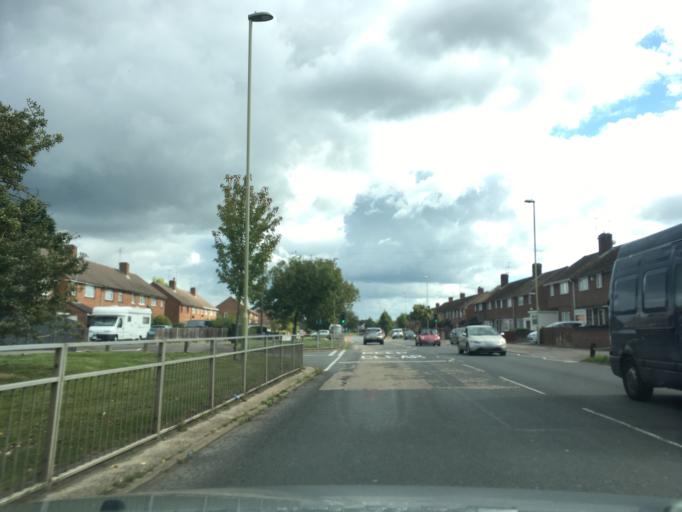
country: GB
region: England
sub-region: Hampshire
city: Havant
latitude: 50.8648
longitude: -1.0032
